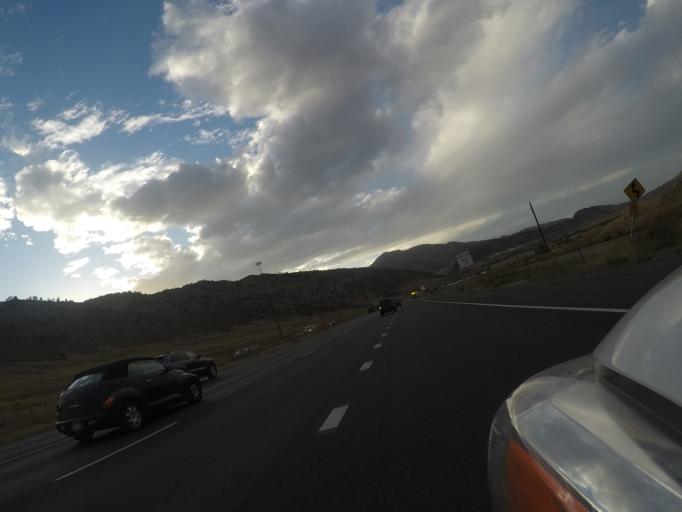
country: US
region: Colorado
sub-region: Jefferson County
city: Indian Hills
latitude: 39.6389
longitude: -105.1689
